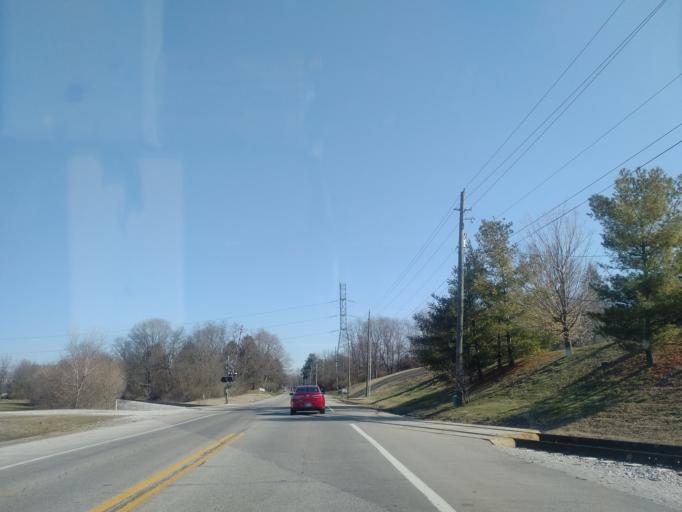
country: US
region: Indiana
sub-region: Marion County
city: Southport
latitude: 39.6737
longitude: -86.1776
